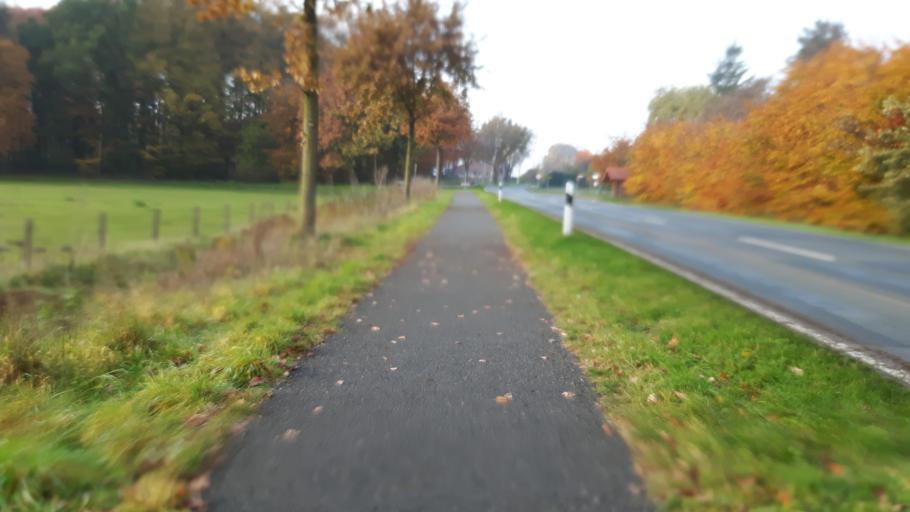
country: DE
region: Lower Saxony
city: Ganderkesee
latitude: 53.0169
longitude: 8.5766
